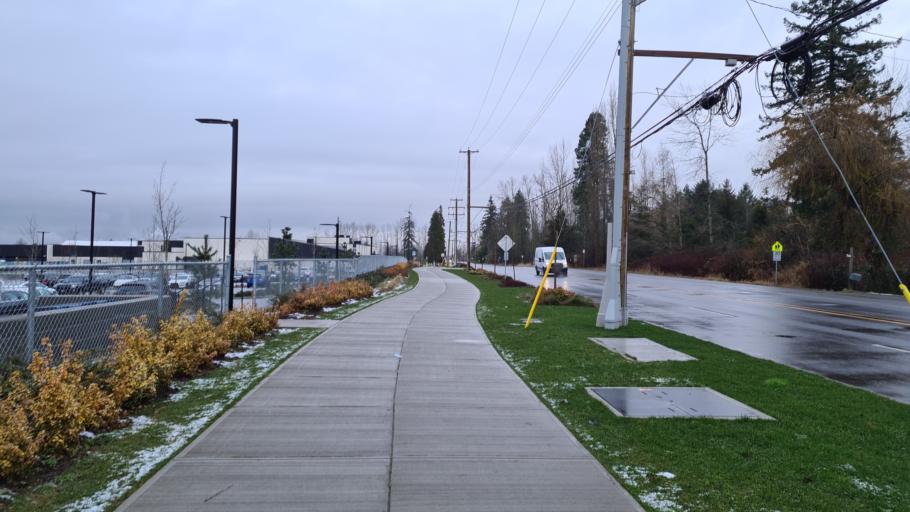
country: CA
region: British Columbia
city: Walnut Grove
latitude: 49.1419
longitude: -122.6617
